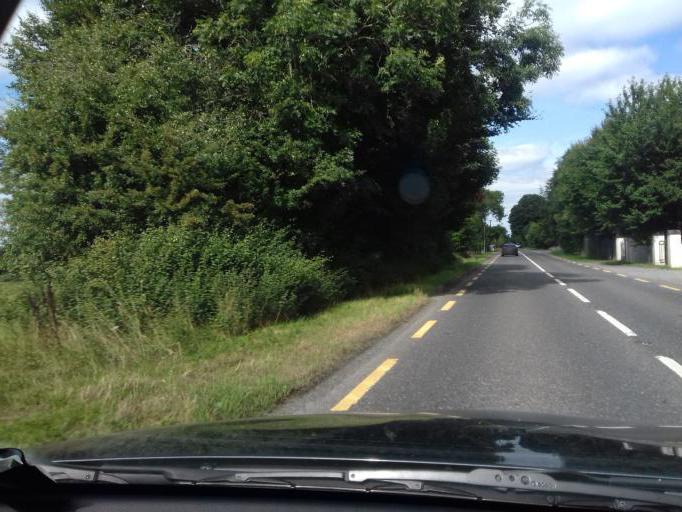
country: IE
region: Leinster
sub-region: Wicklow
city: Valleymount
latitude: 53.1058
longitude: -6.6037
